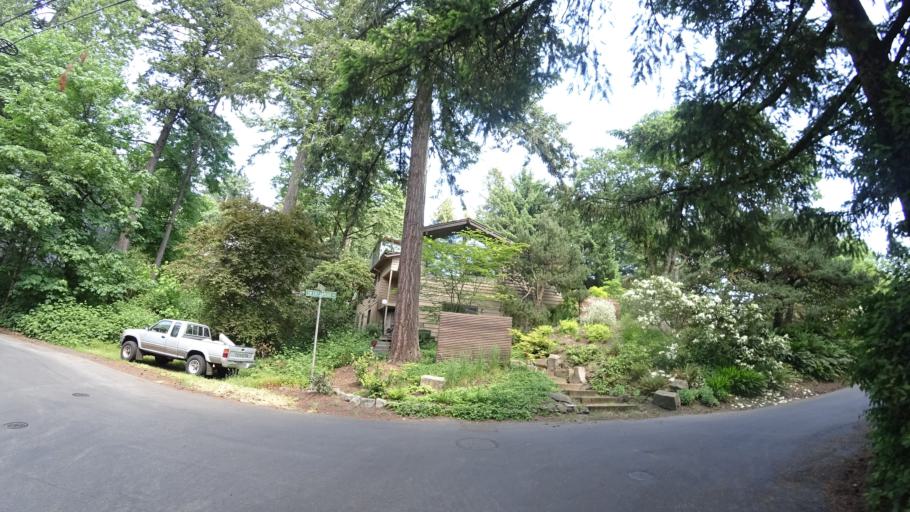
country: US
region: Oregon
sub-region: Multnomah County
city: Portland
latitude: 45.4929
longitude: -122.7056
